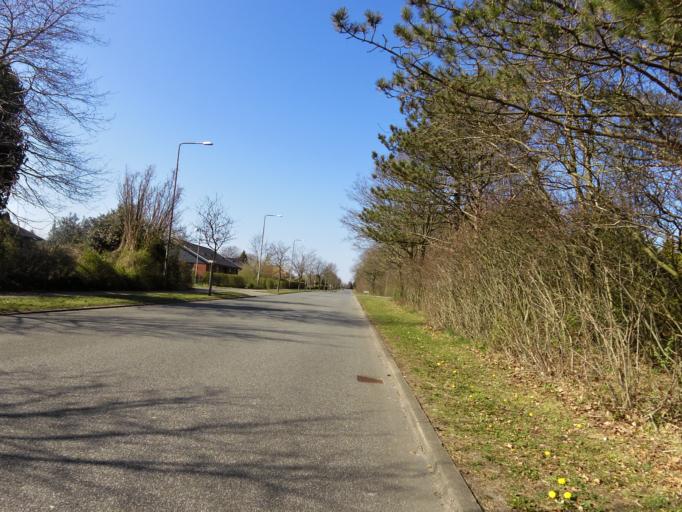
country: DK
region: South Denmark
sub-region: Esbjerg Kommune
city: Ribe
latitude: 55.3447
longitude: 8.7873
